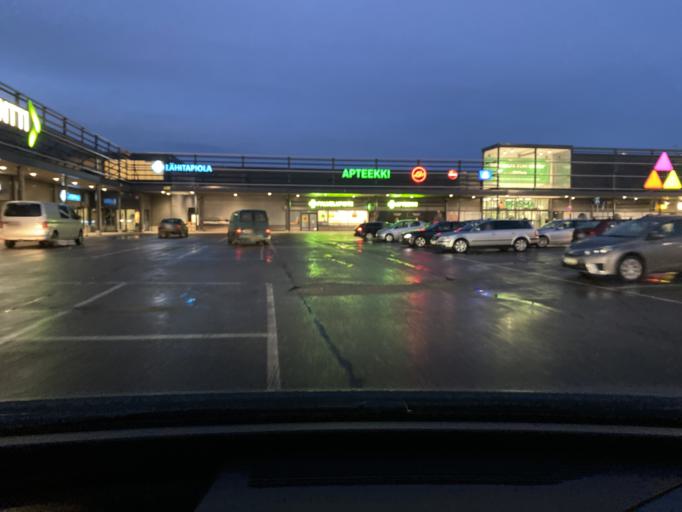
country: FI
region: Varsinais-Suomi
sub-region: Loimaa
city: Loimaa
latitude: 60.8563
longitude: 23.0442
